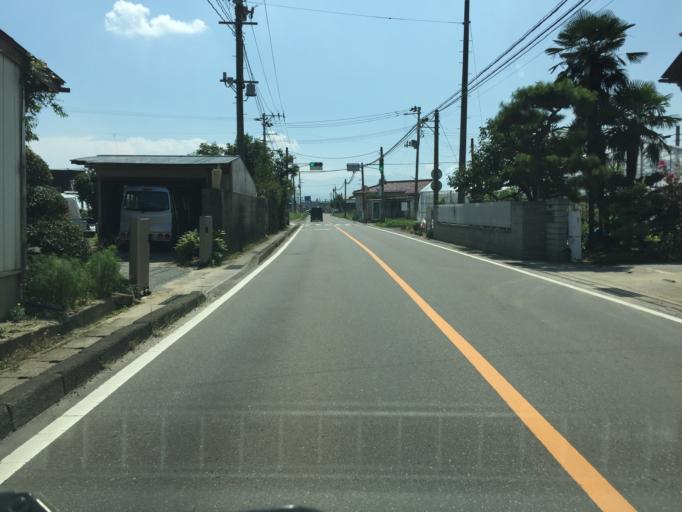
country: JP
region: Fukushima
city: Hobaramachi
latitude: 37.7894
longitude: 140.5093
